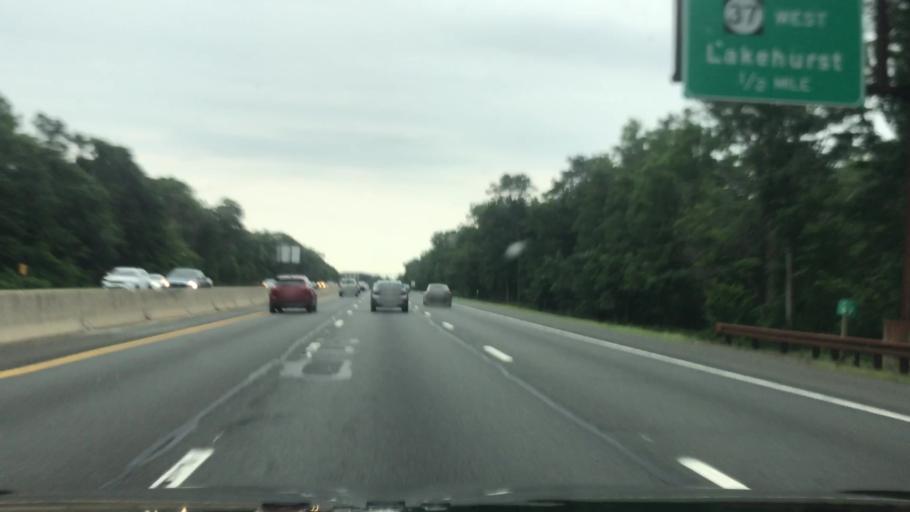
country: US
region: New Jersey
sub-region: Ocean County
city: Silver Ridge
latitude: 39.9735
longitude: -74.2104
